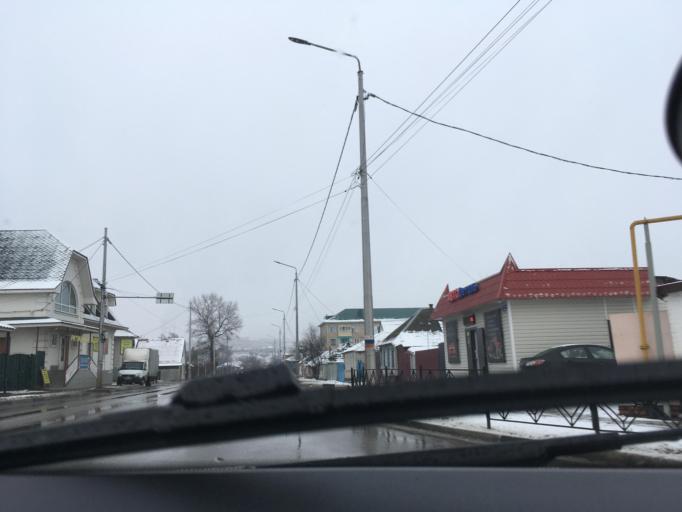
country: RU
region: Belgorod
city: Valuyki
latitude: 50.2043
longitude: 38.1057
